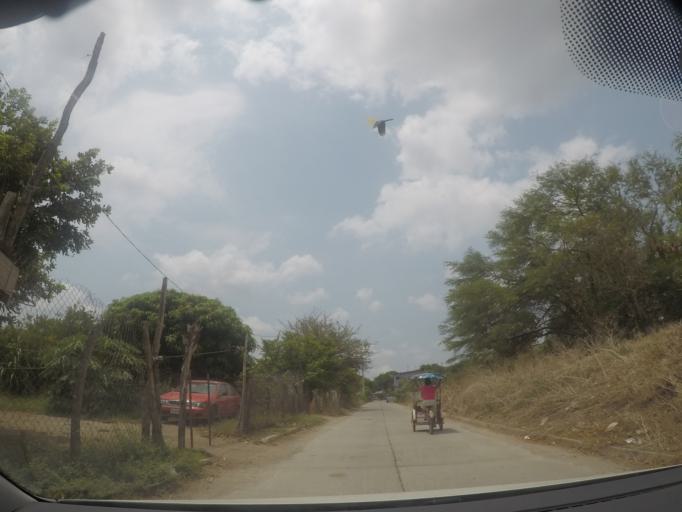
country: MX
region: Oaxaca
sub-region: El Espinal
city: El Espinal
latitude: 16.4904
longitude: -95.0462
